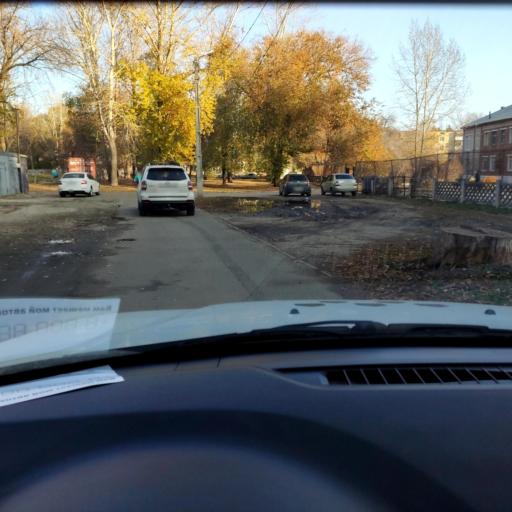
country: RU
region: Samara
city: Tol'yatti
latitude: 53.5134
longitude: 49.4192
